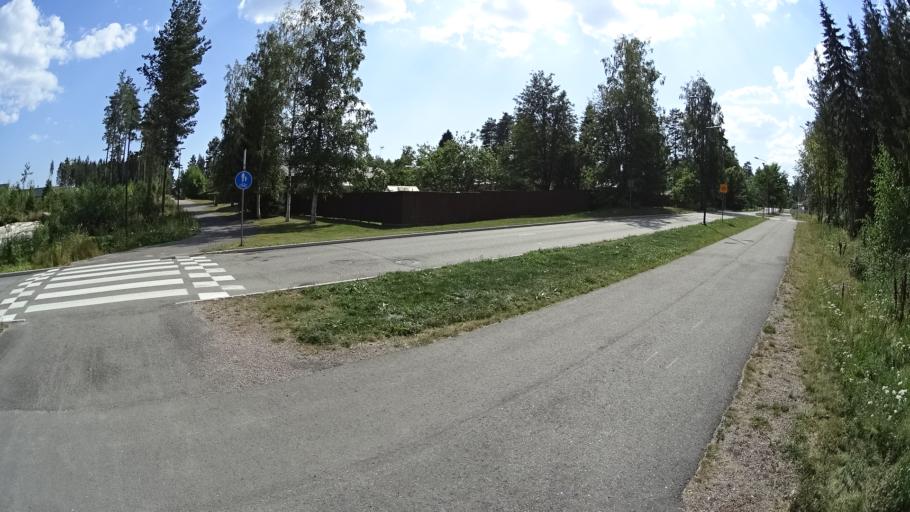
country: FI
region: Uusimaa
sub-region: Porvoo
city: Porvoo
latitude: 60.3868
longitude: 25.7103
